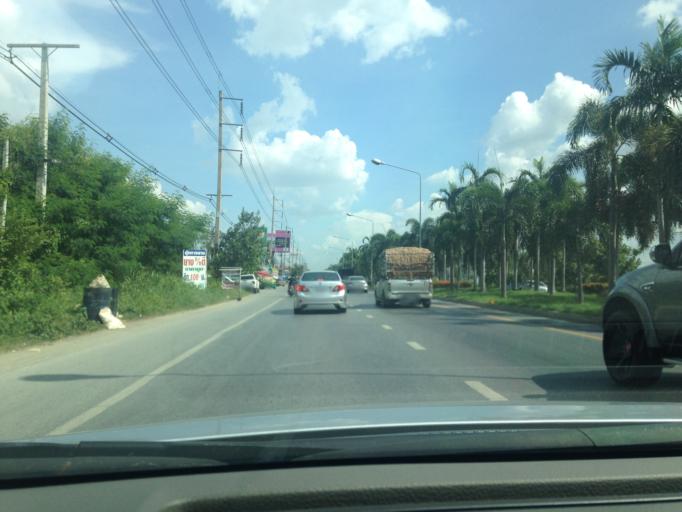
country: TH
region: Phra Nakhon Si Ayutthaya
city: Ban Bang Kadi Pathum Thani
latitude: 14.0000
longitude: 100.5709
